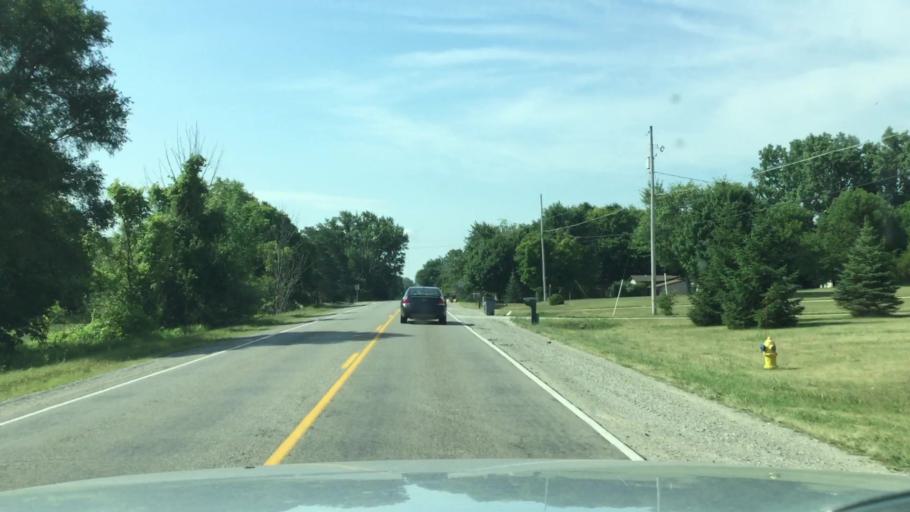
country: US
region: Michigan
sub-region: Genesee County
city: Flushing
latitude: 43.1009
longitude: -83.8137
